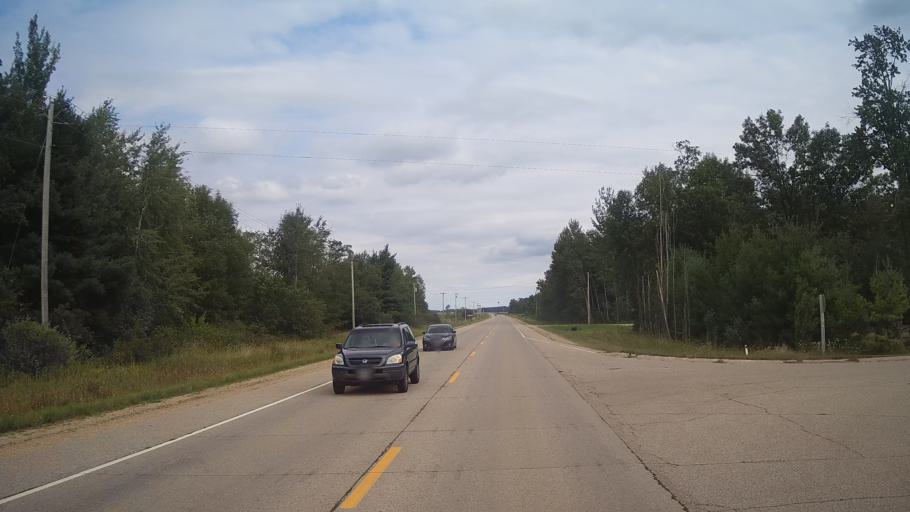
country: US
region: Wisconsin
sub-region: Waushara County
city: Redgranite
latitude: 44.0375
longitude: -89.0719
